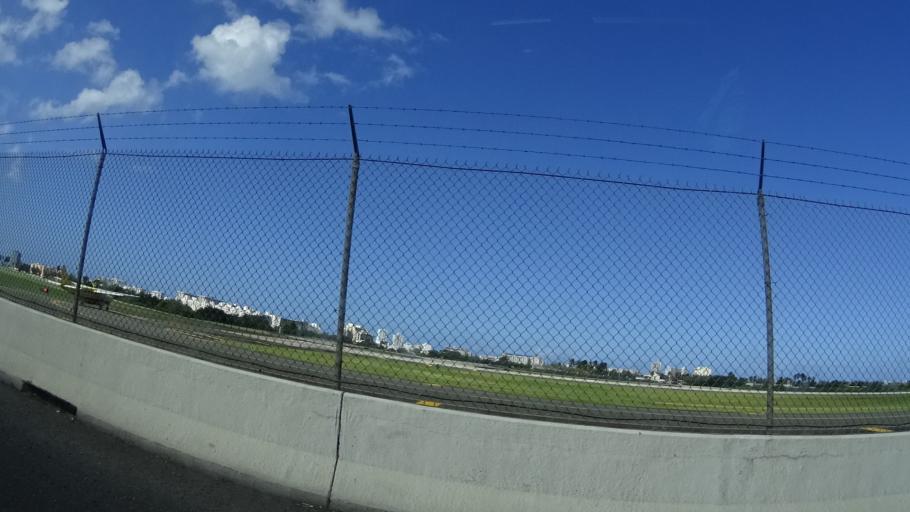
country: PR
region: Carolina
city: Carolina
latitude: 18.4324
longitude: -66.0127
